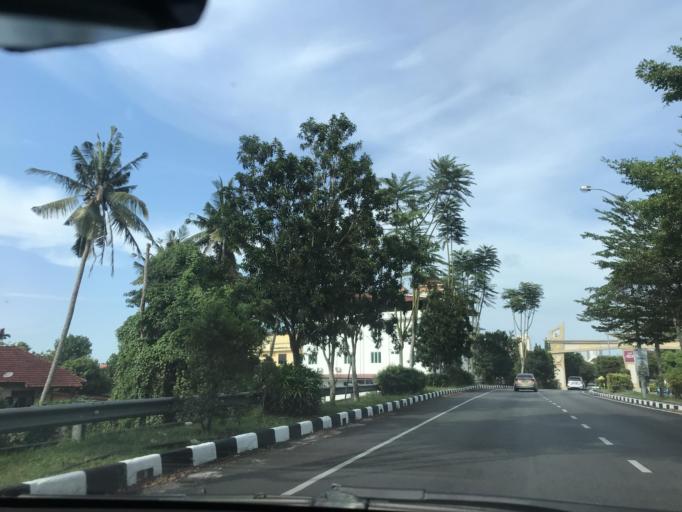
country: MY
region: Kelantan
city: Kota Bharu
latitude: 6.1109
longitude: 102.2358
